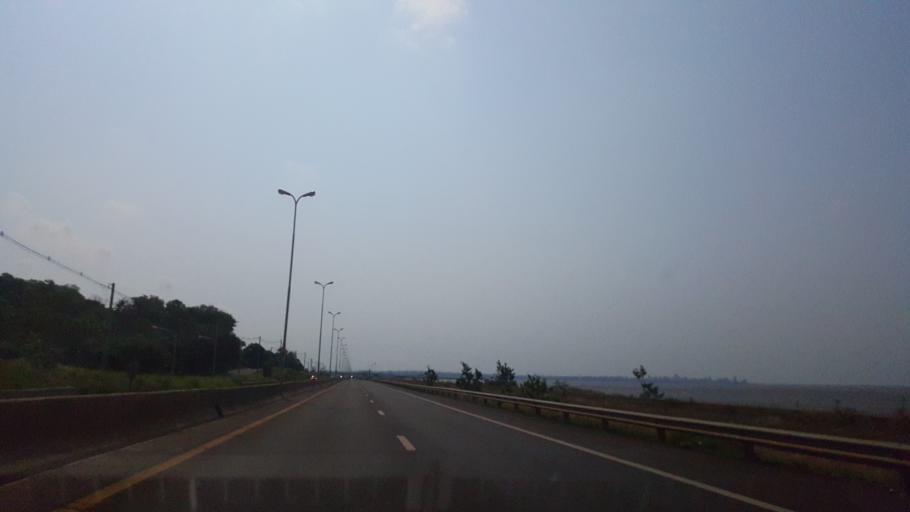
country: AR
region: Misiones
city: Garupa
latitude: -27.4411
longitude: -55.8517
